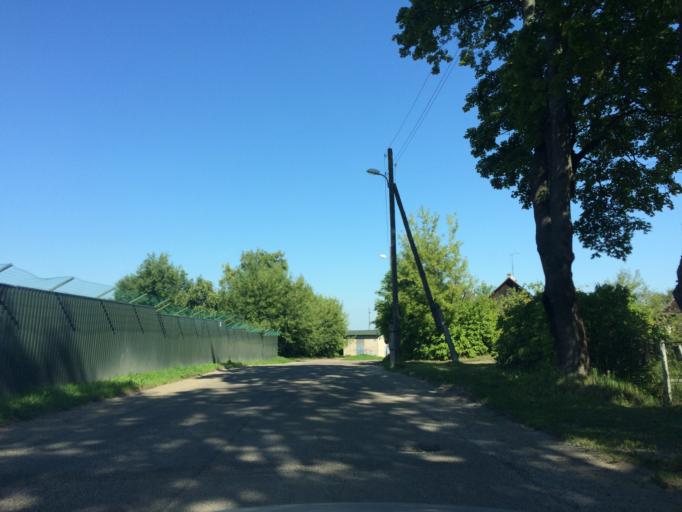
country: LV
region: Rezekne
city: Rezekne
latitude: 56.5054
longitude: 27.3190
